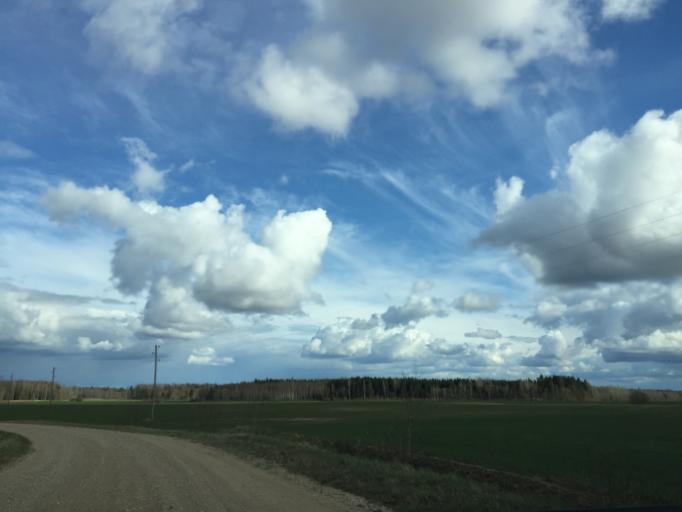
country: LV
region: Burtnieki
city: Matisi
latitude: 57.6119
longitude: 25.0233
